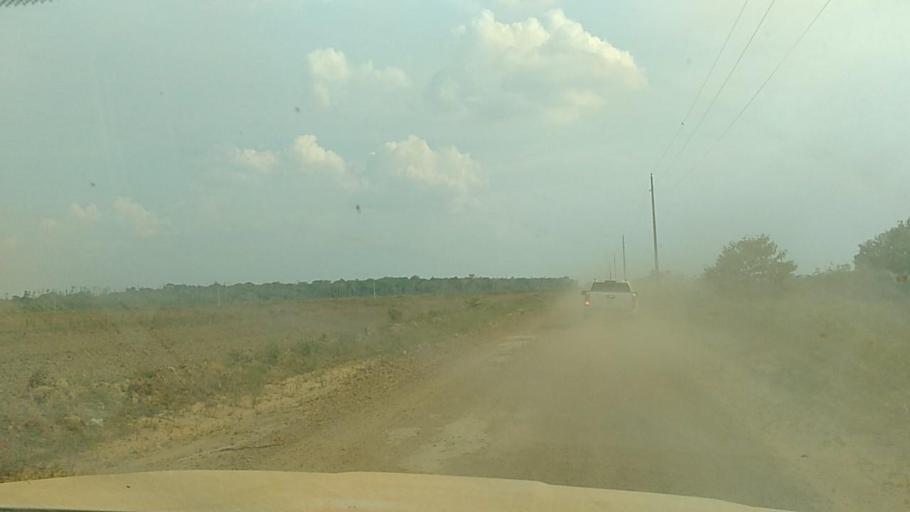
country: BR
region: Rondonia
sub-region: Porto Velho
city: Porto Velho
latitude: -8.6697
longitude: -64.0238
